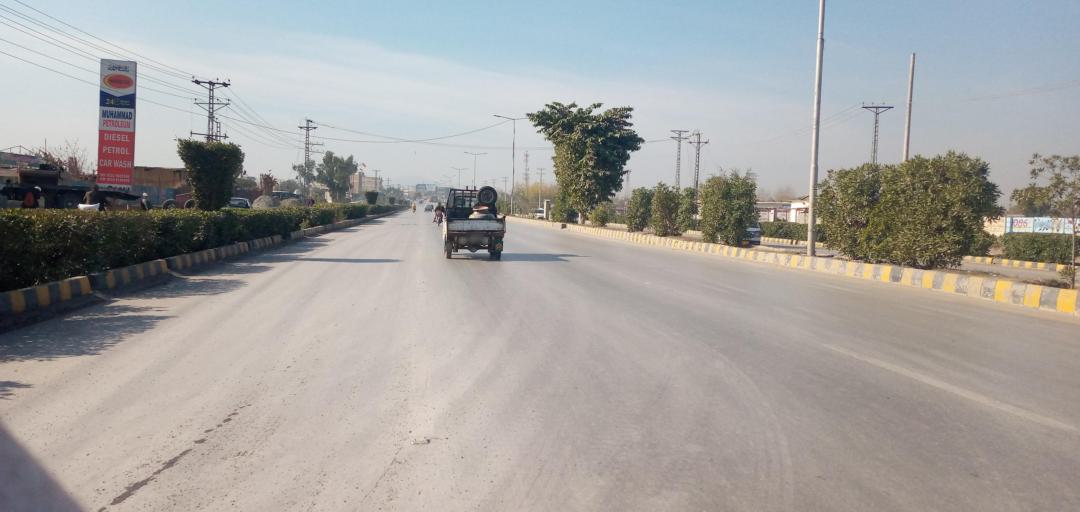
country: PK
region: Khyber Pakhtunkhwa
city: Peshawar
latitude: 33.9612
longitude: 71.5157
